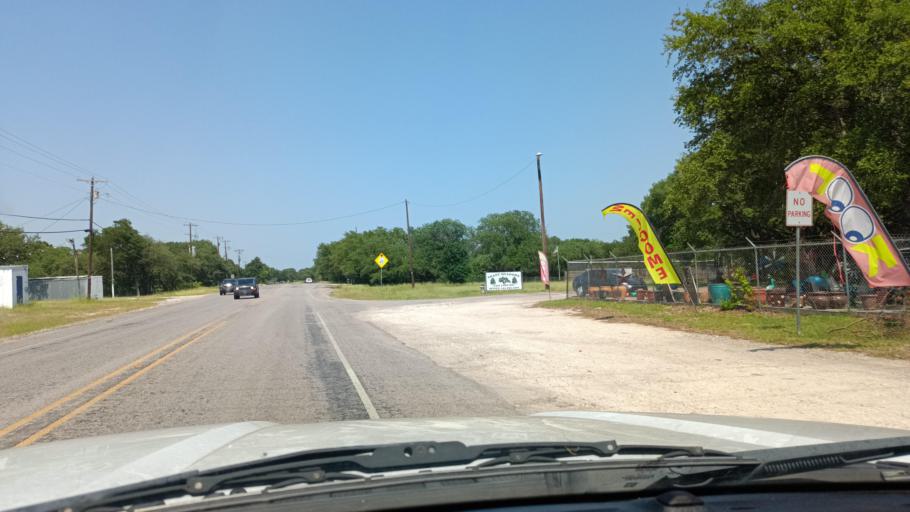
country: US
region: Texas
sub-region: Bell County
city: Belton
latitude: 31.1022
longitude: -97.4861
